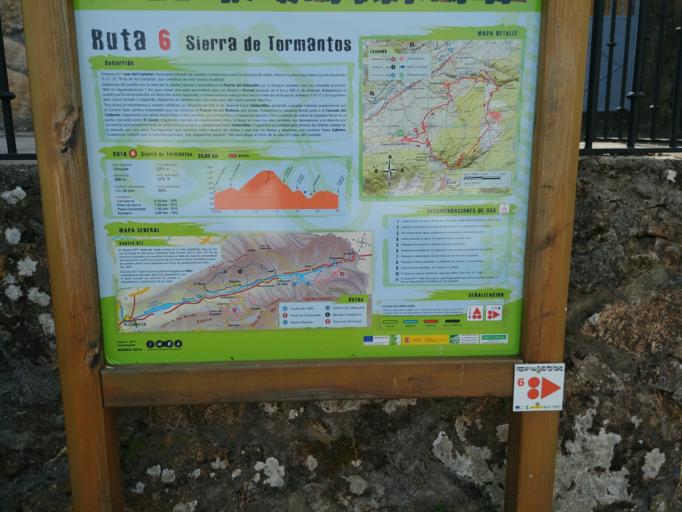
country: ES
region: Extremadura
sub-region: Provincia de Caceres
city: Casas del Castanar
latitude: 40.1071
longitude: -5.9027
